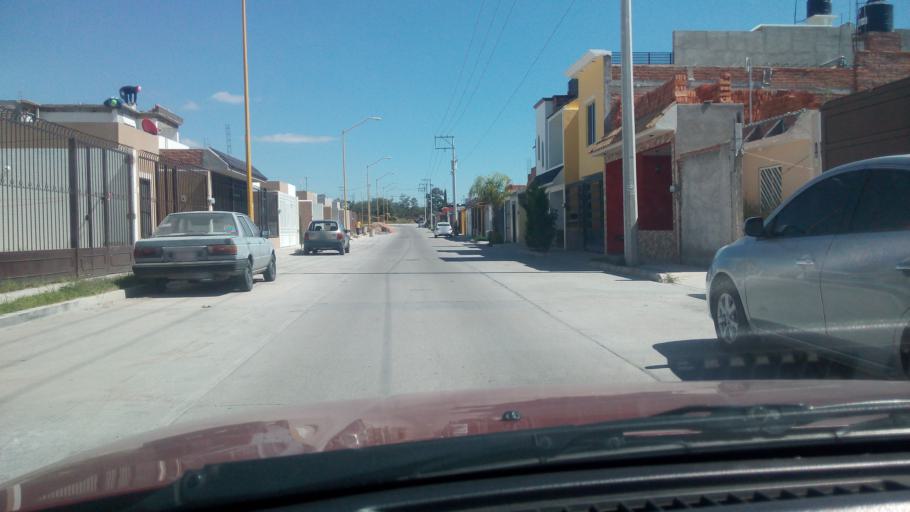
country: MX
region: Aguascalientes
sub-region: Aguascalientes
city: San Sebastian [Fraccionamiento]
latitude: 21.8365
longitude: -102.2963
